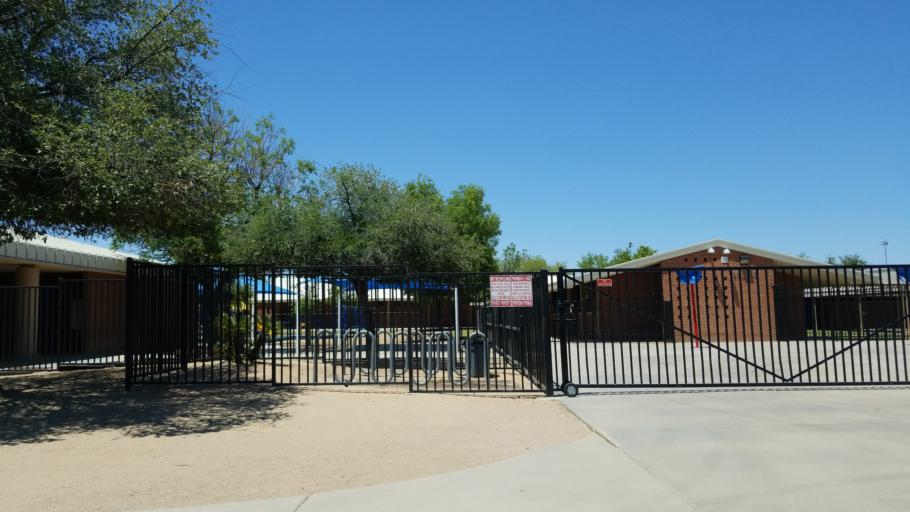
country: US
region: Arizona
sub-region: Maricopa County
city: Phoenix
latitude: 33.5169
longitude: -112.0926
